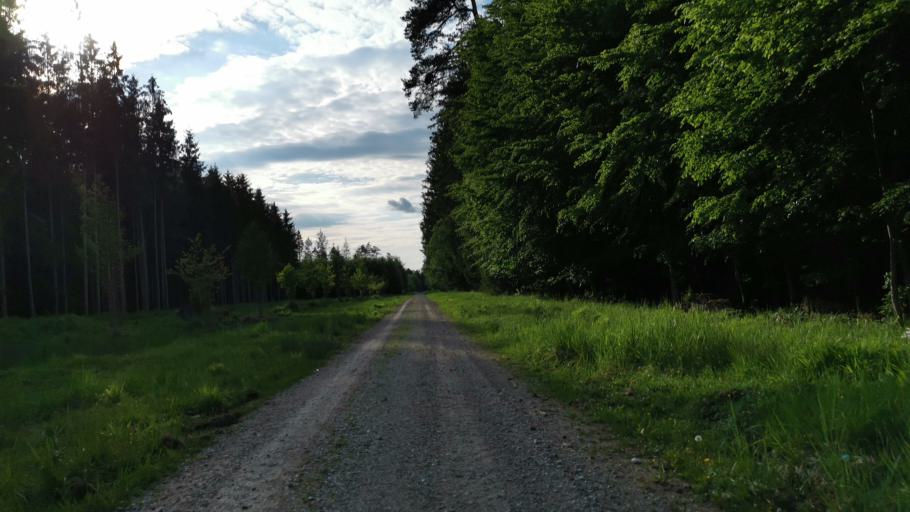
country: DE
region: Bavaria
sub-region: Upper Bavaria
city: Neuried
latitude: 48.0604
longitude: 11.4836
